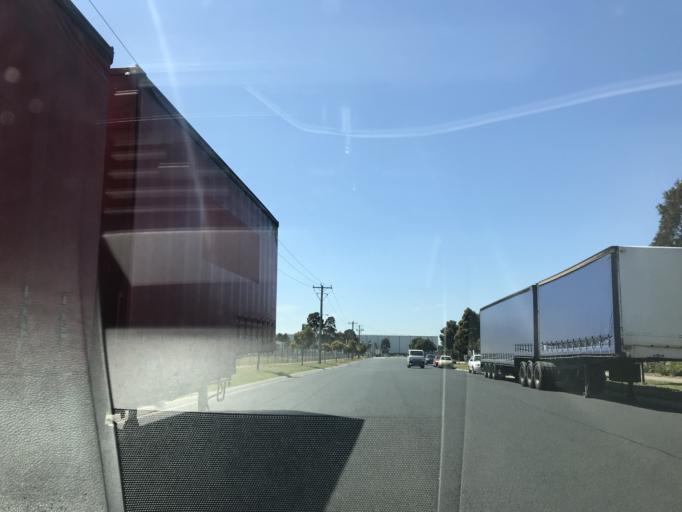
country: AU
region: Victoria
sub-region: Wyndham
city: Truganina
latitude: -37.8189
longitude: 144.7723
